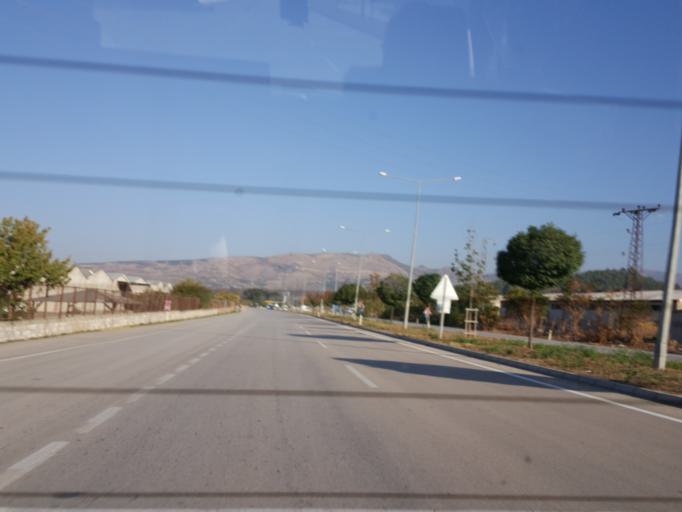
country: TR
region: Amasya
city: Amasya
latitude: 40.5613
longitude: 35.7911
